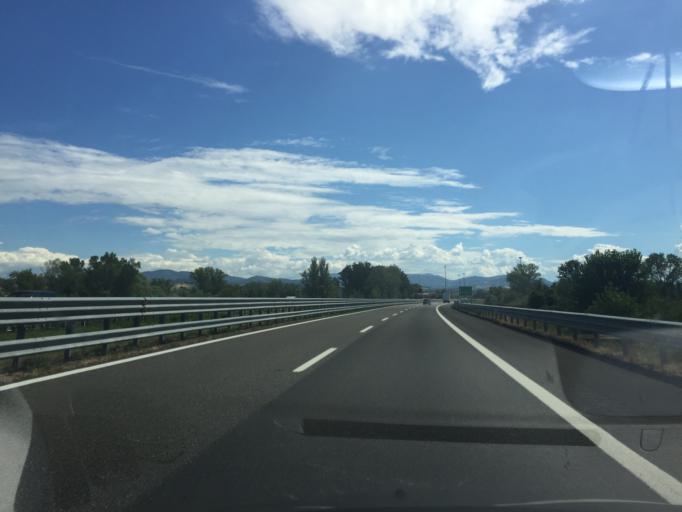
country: IT
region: Emilia-Romagna
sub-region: Provincia di Parma
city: Gaiano
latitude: 44.7494
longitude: 10.1665
